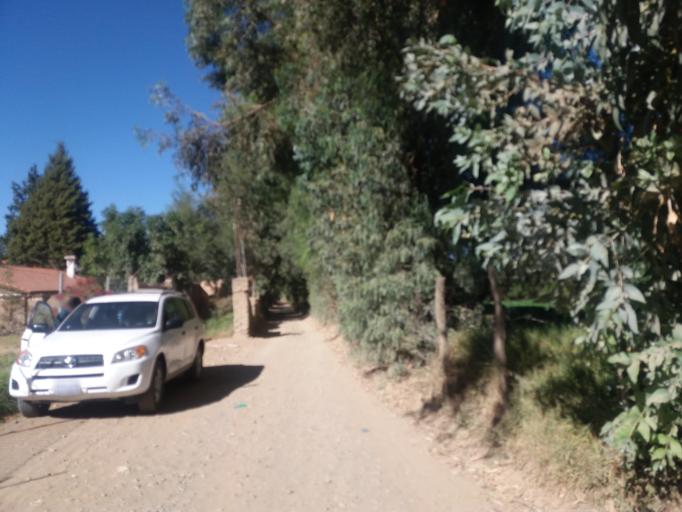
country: BO
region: Cochabamba
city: Cochabamba
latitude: -17.3457
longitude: -66.2172
